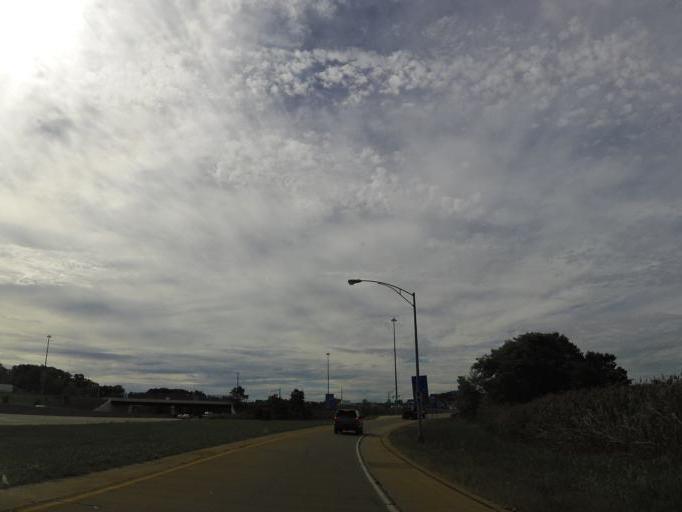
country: US
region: Ohio
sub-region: Summit County
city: Silver Lake
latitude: 41.1832
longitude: -81.4780
